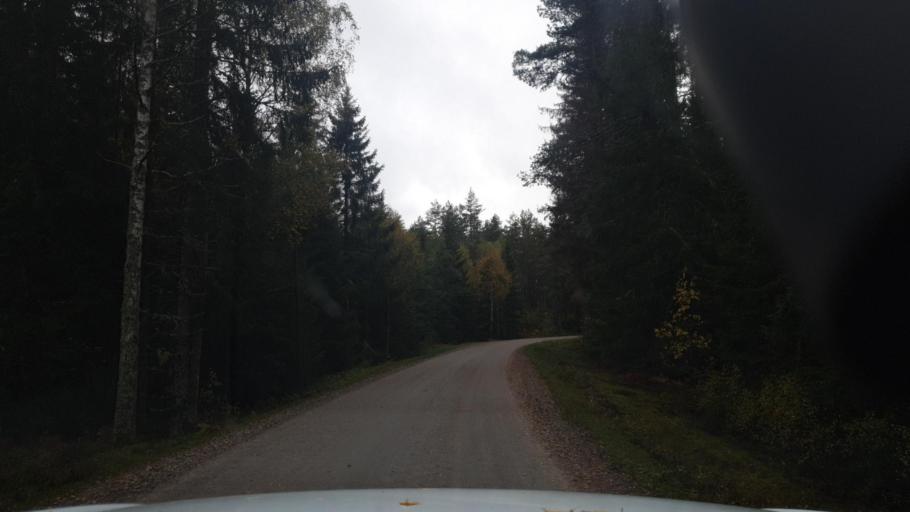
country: SE
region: Vaermland
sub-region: Karlstads Kommun
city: Edsvalla
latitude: 59.5370
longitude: 12.9979
